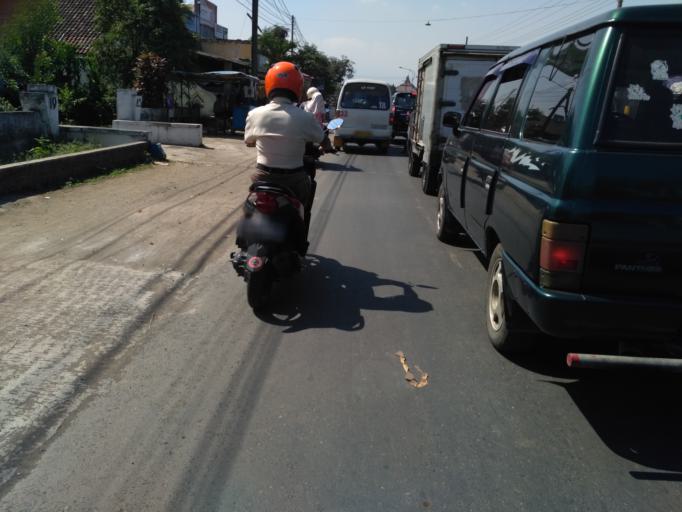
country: ID
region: East Java
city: Tamiajeng
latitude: -7.9541
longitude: 112.7024
